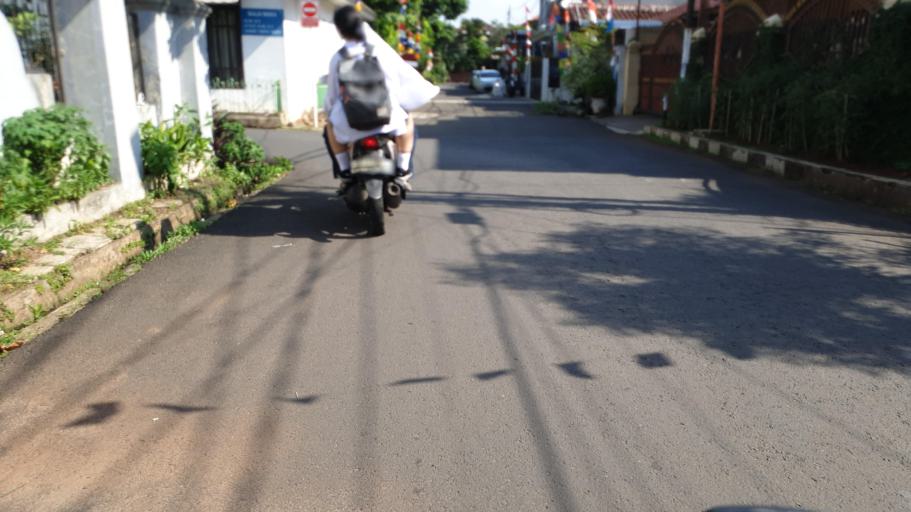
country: ID
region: Jakarta Raya
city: Jakarta
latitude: -6.2892
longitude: 106.8392
